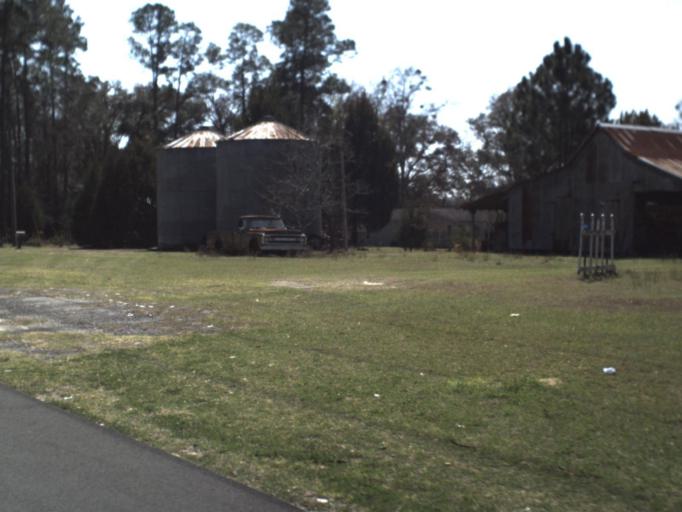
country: US
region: Florida
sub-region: Jackson County
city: Malone
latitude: 30.8343
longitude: -85.0574
